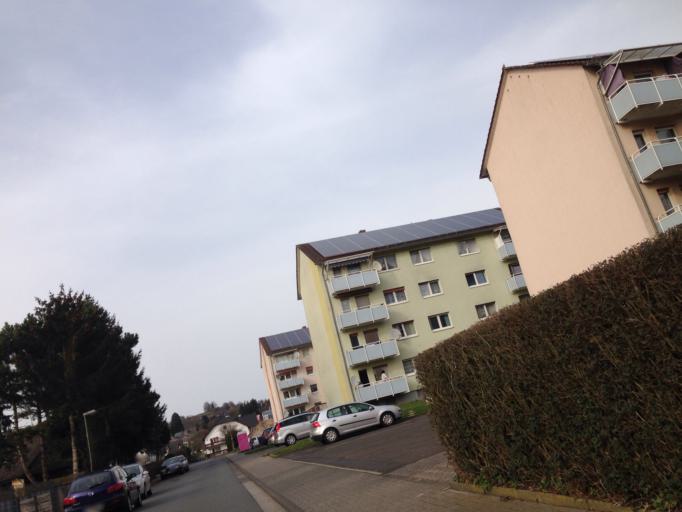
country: DE
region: Hesse
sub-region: Regierungsbezirk Giessen
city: Grossen Buseck
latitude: 50.6054
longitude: 8.7933
